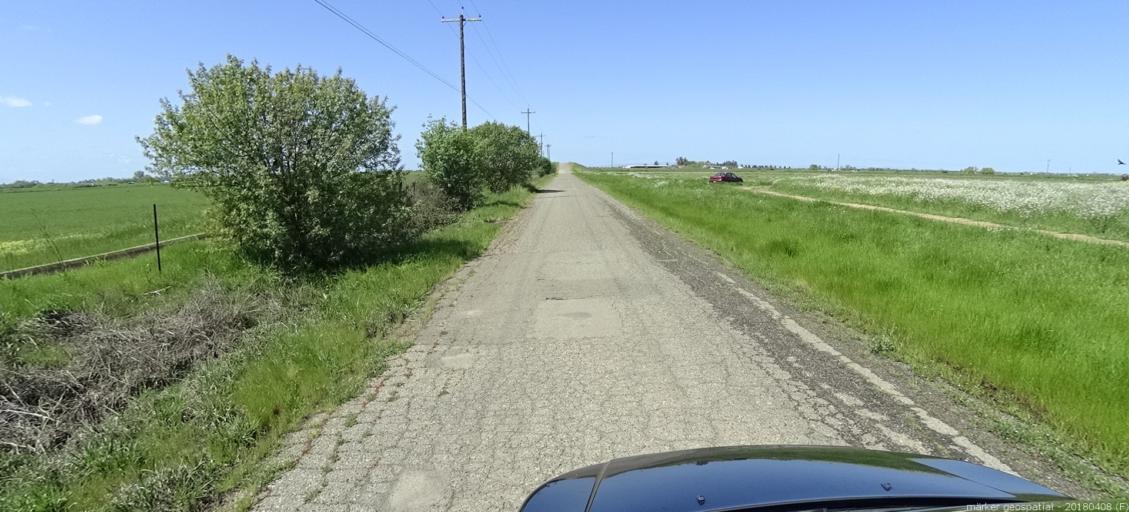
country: US
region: California
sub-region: San Joaquin County
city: Thornton
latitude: 38.2987
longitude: -121.4546
